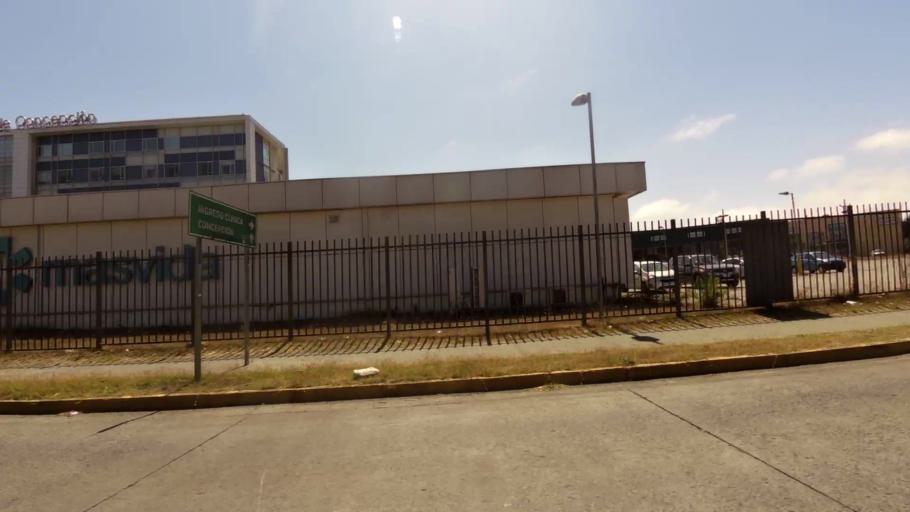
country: CL
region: Biobio
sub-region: Provincia de Concepcion
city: Concepcion
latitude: -36.8002
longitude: -73.0706
